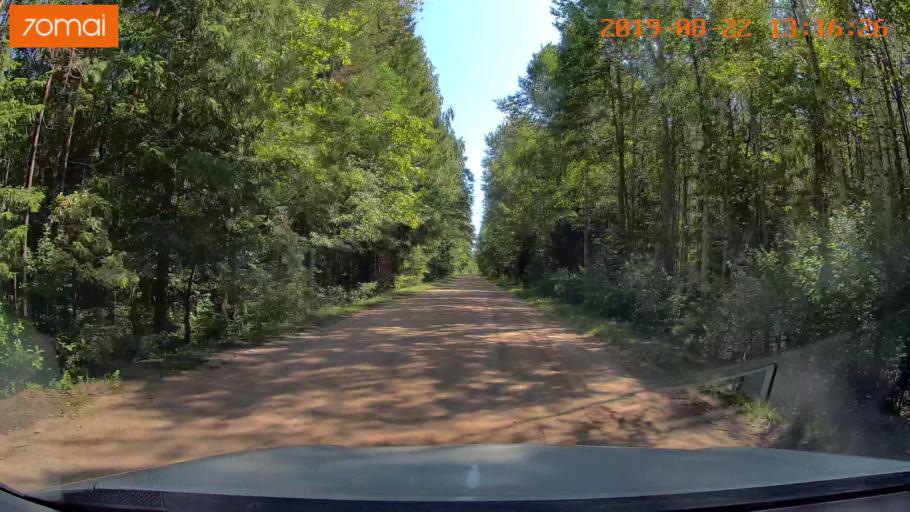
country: BY
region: Minsk
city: Prawdzinski
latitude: 53.2558
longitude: 27.9108
